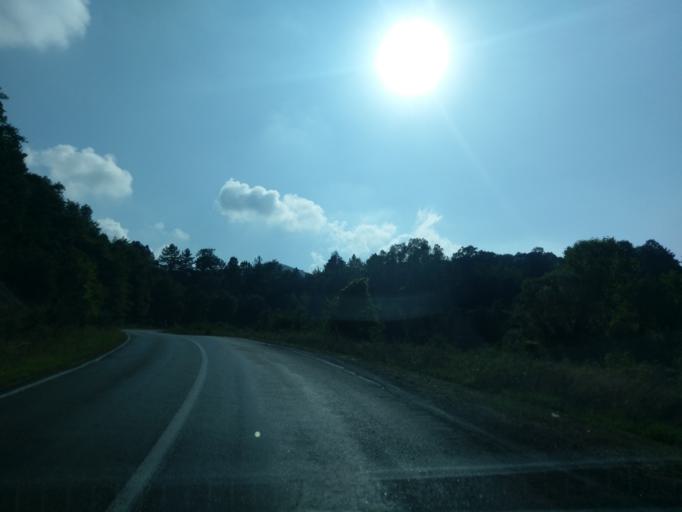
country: TR
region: Sinop
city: Yenikonak
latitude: 41.9412
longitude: 34.7158
